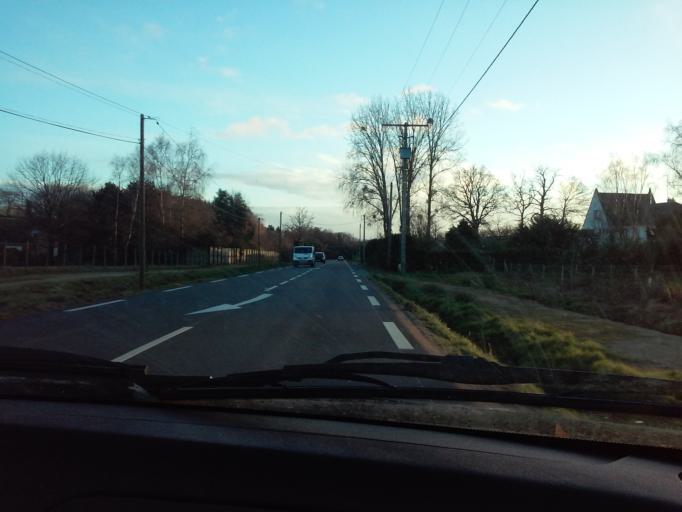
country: FR
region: Brittany
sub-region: Departement d'Ille-et-Vilaine
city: Vitre
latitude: 48.1045
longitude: -1.2216
